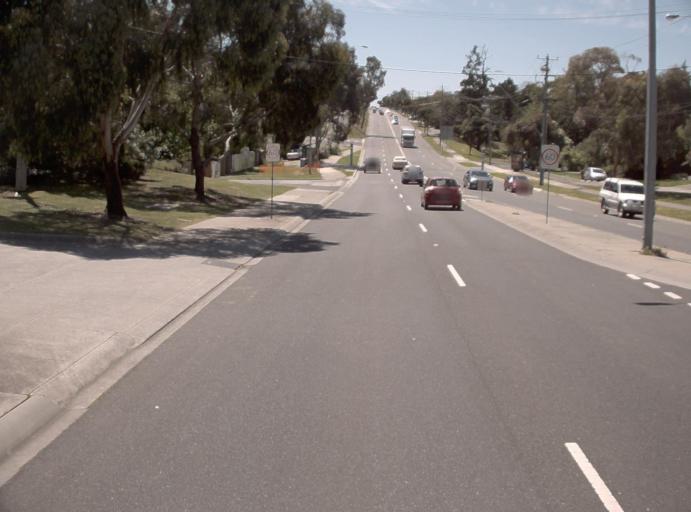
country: AU
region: Victoria
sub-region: Whitehorse
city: Blackburn North
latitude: -37.7999
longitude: 145.1598
